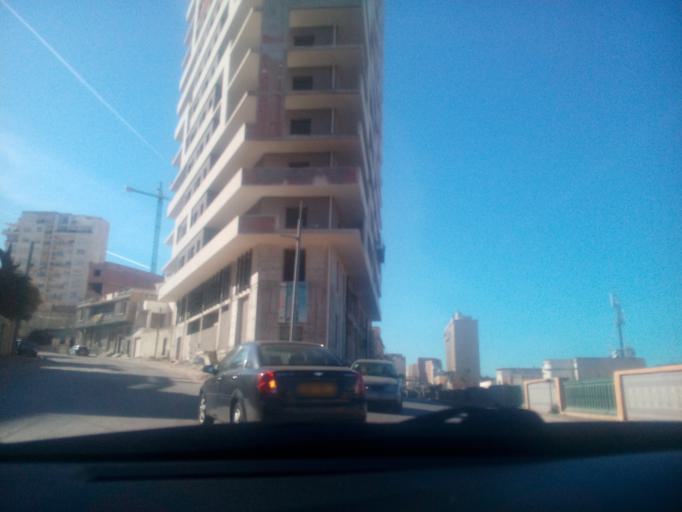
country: DZ
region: Oran
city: Oran
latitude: 35.7049
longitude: -0.6245
